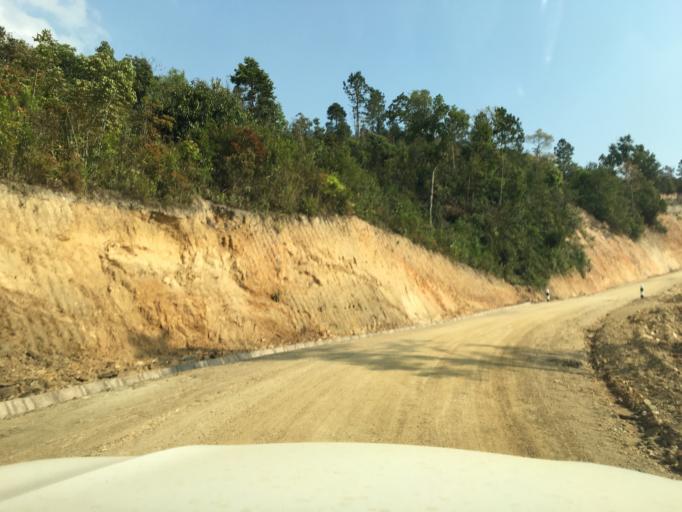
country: LA
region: Houaphan
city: Huameung
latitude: 20.1933
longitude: 103.8342
